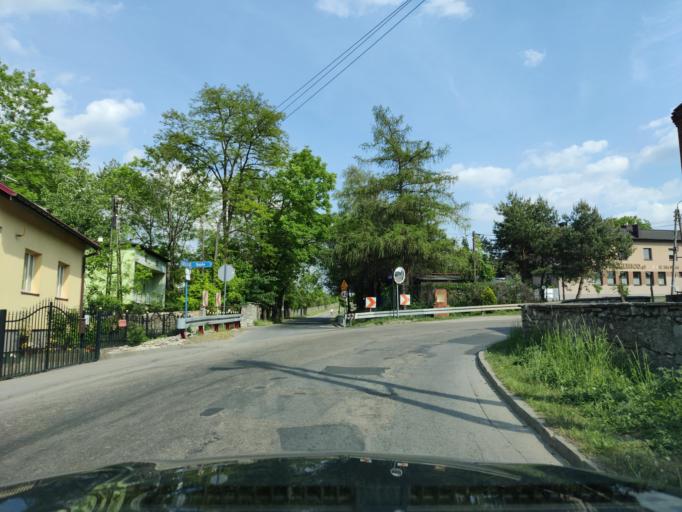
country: PL
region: Silesian Voivodeship
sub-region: Dabrowa Gornicza
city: Dabrowa Gornicza
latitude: 50.3910
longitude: 19.2419
